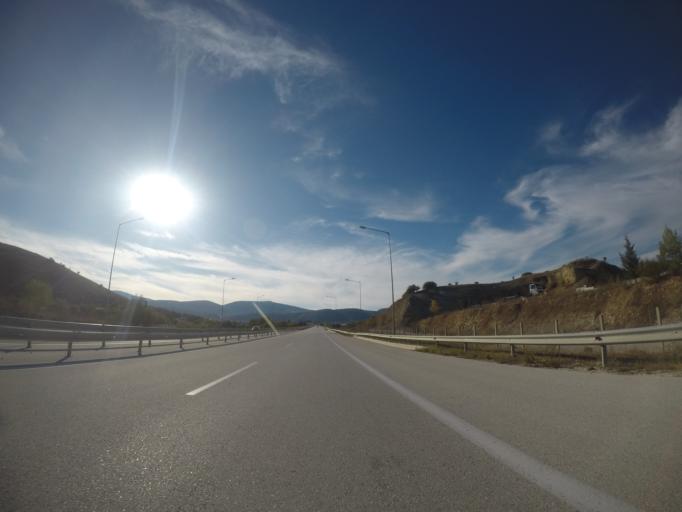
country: GR
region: Epirus
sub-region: Nomos Ioanninon
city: Katsikas
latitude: 39.6033
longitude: 20.8868
